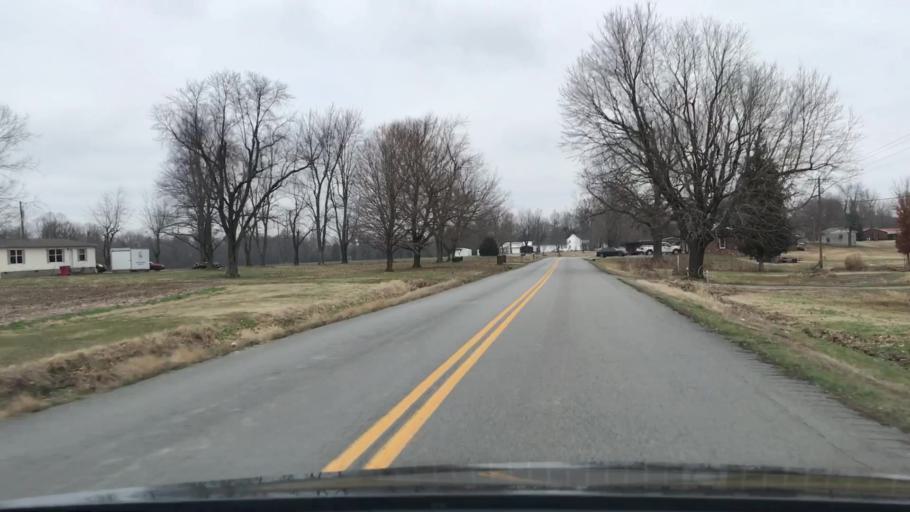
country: US
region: Kentucky
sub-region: Muhlenberg County
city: Morehead
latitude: 37.3374
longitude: -87.2212
